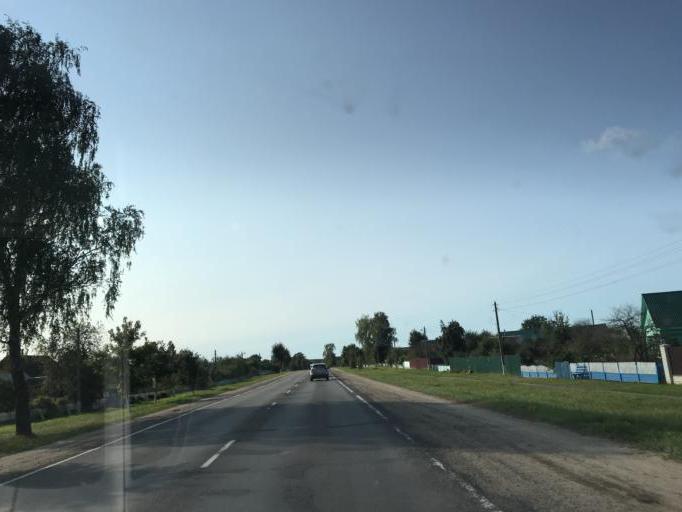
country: BY
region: Mogilev
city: Buynichy
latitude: 53.8377
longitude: 30.2471
